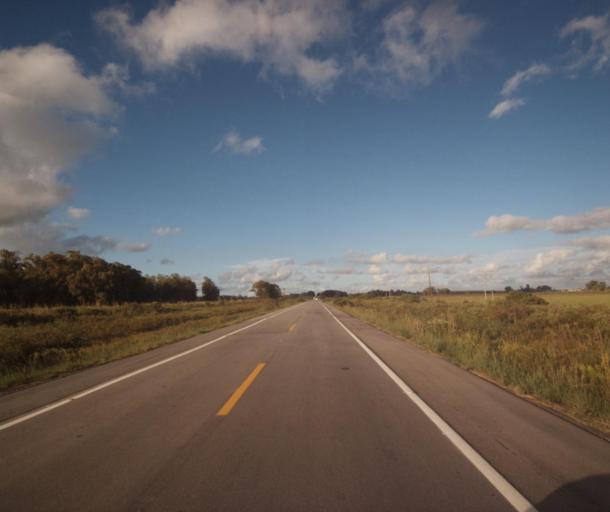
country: BR
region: Rio Grande do Sul
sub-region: Rio Grande
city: Rio Grande
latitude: -32.1334
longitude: -52.3729
